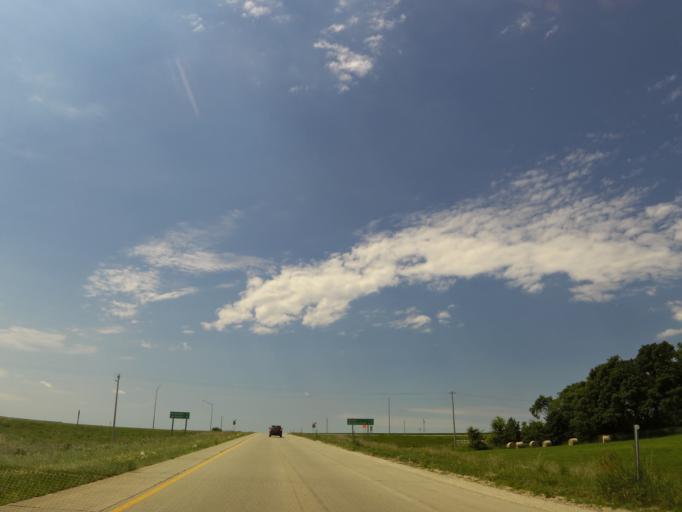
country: US
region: Iowa
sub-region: Bremer County
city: Denver
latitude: 42.7162
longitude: -92.3382
